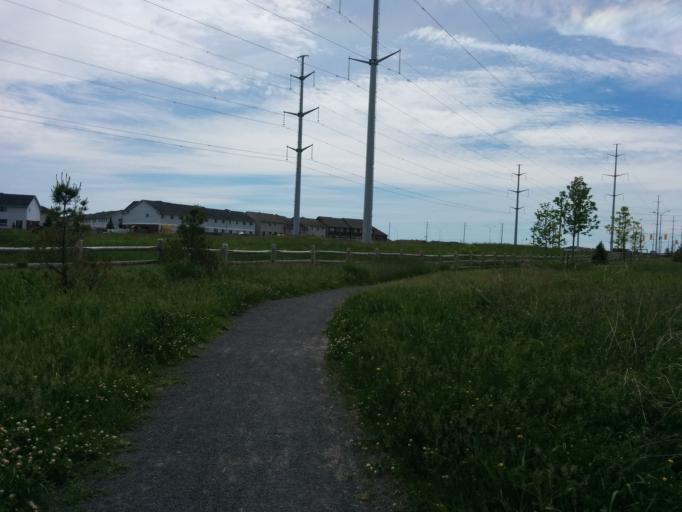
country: CA
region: Ontario
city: Clarence-Rockland
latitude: 45.4786
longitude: -75.4570
